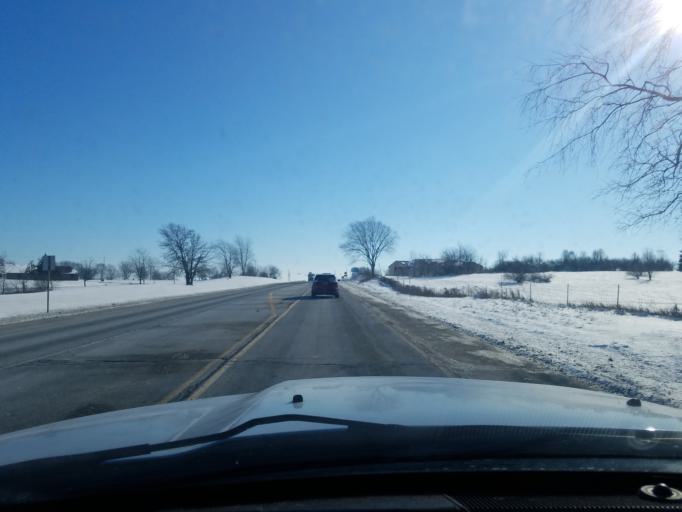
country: US
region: Indiana
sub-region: Noble County
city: Kendallville
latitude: 41.4472
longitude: -85.2357
